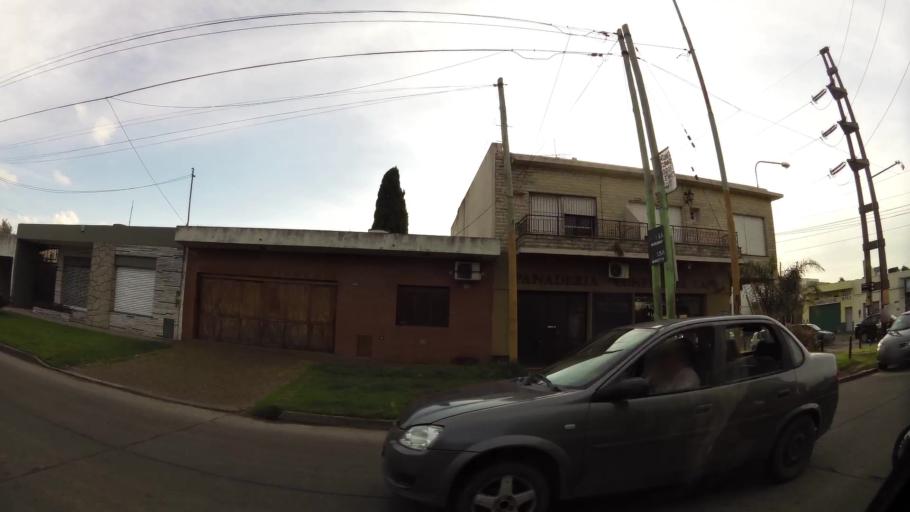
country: AR
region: Buenos Aires
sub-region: Partido de Quilmes
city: Quilmes
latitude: -34.7378
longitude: -58.2711
